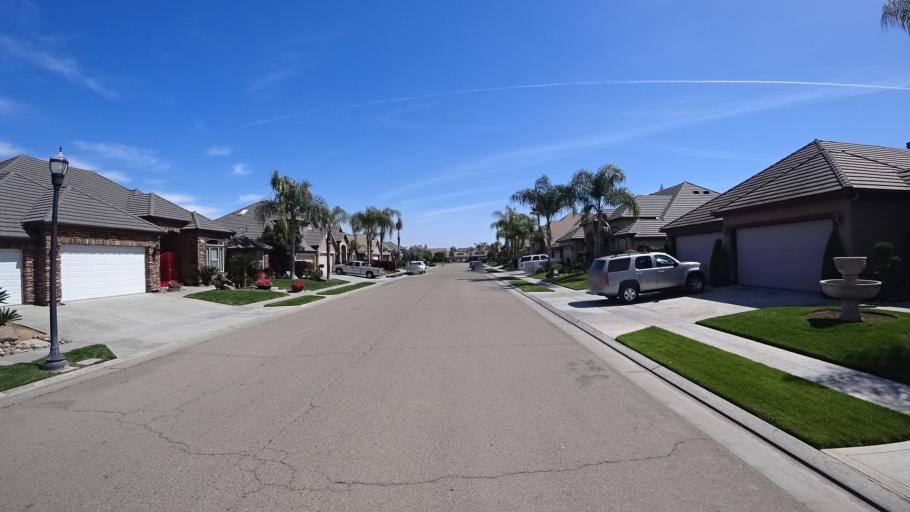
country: US
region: California
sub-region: Fresno County
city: Biola
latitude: 36.8193
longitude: -119.9132
